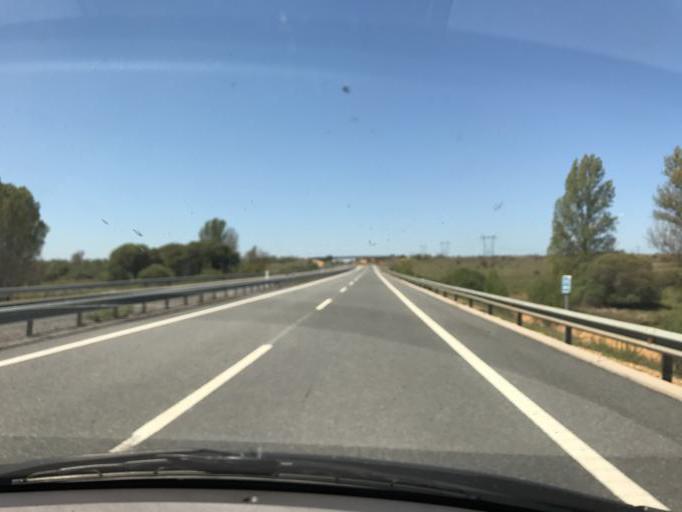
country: ES
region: Castille and Leon
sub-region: Provincia de Leon
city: Valverde de la Virgen
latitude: 42.5610
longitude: -5.6778
